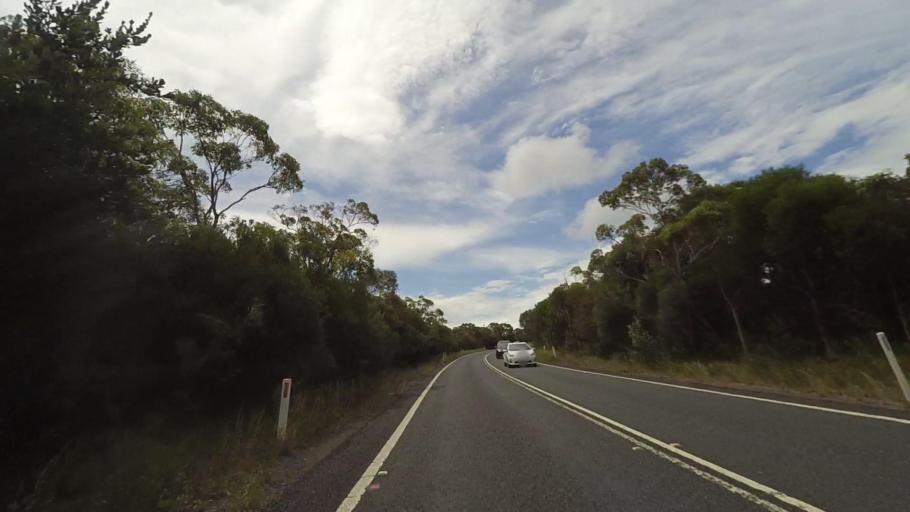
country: AU
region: New South Wales
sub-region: Sutherland Shire
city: Heathcote
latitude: -34.1127
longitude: 151.0600
